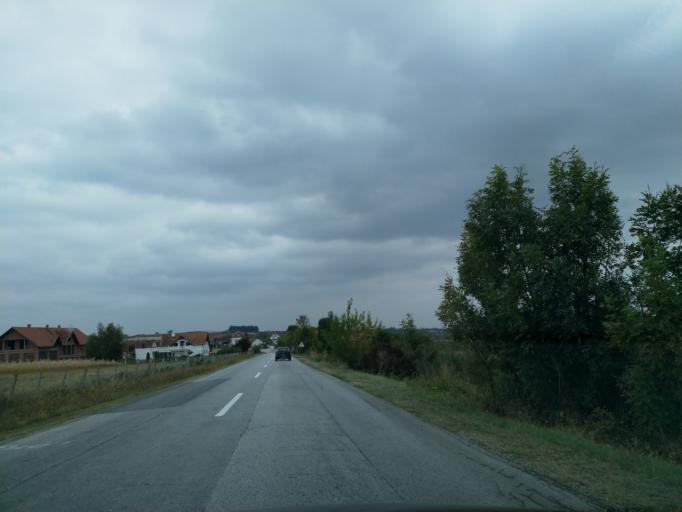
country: RS
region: Central Serbia
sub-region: Sumadijski Okrug
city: Topola
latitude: 44.1792
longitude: 20.7393
